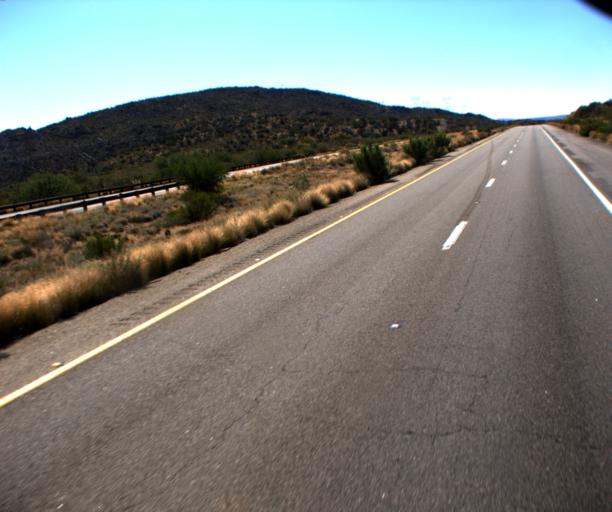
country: US
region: Arizona
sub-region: Yavapai County
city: Bagdad
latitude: 34.4232
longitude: -113.2400
